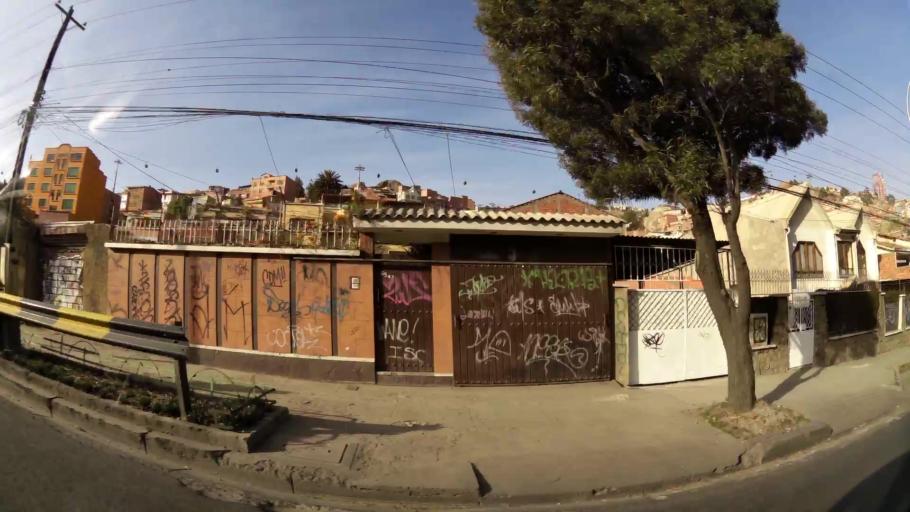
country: BO
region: La Paz
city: La Paz
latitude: -16.5325
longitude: -68.0982
